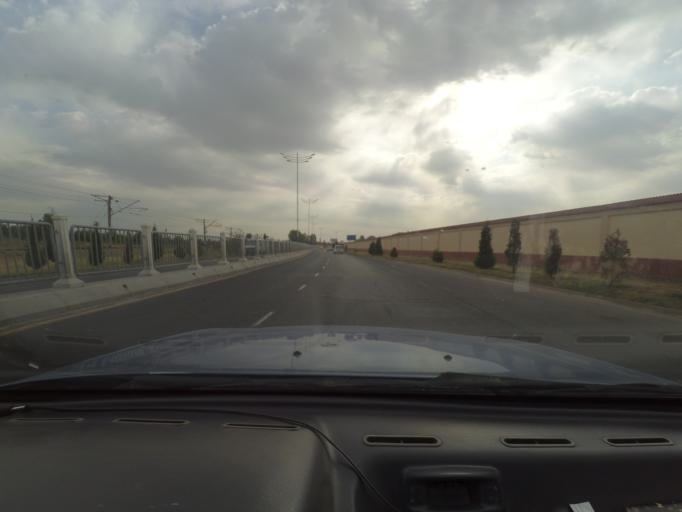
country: UZ
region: Toshkent
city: Salor
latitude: 41.3690
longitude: 69.4106
